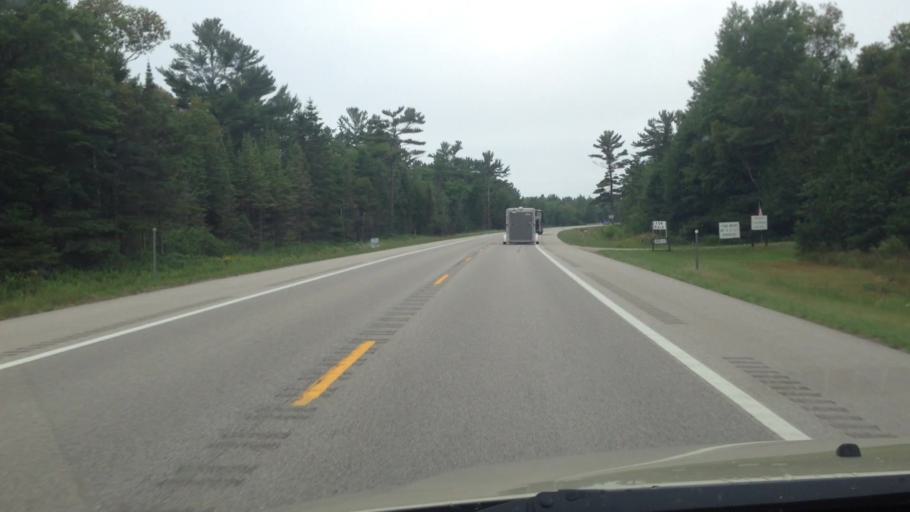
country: US
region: Michigan
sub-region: Luce County
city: Newberry
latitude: 46.0656
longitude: -85.2587
